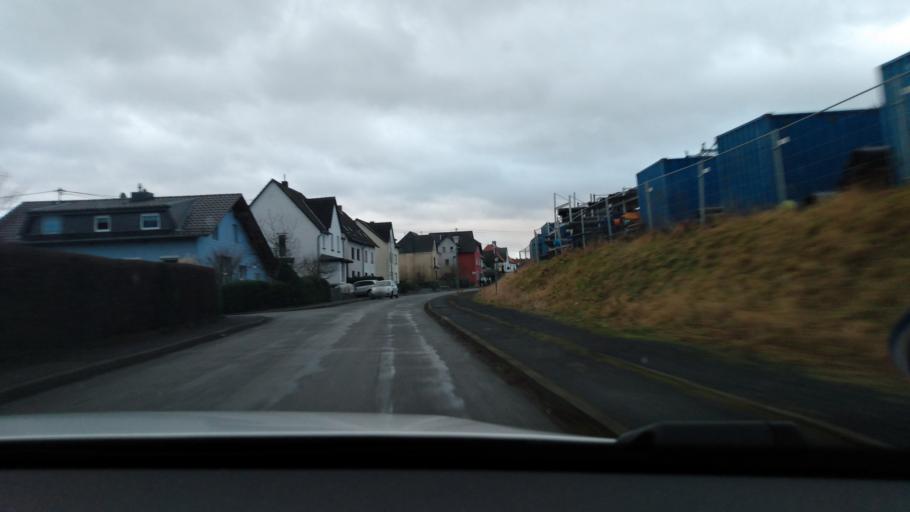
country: DE
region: Rheinland-Pfalz
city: Vettelschoss
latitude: 50.6168
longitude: 7.3117
